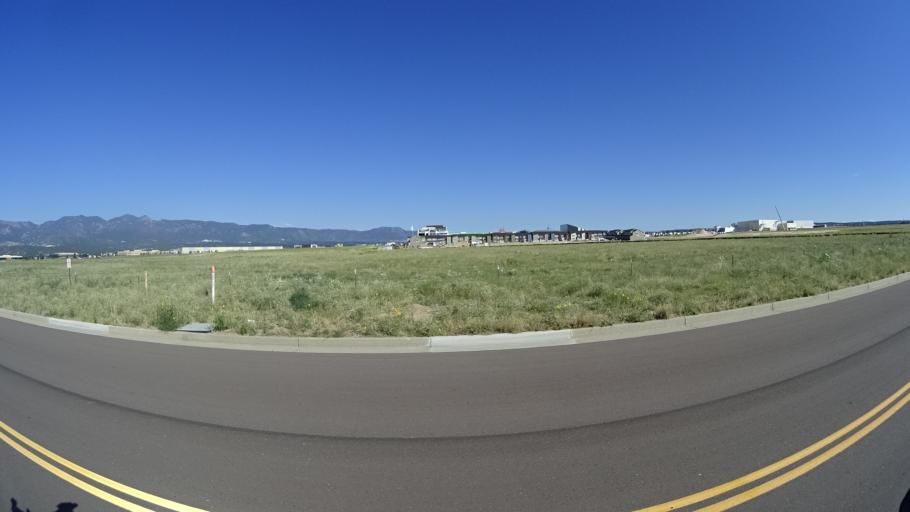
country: US
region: Colorado
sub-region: El Paso County
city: Gleneagle
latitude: 38.9831
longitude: -104.7903
